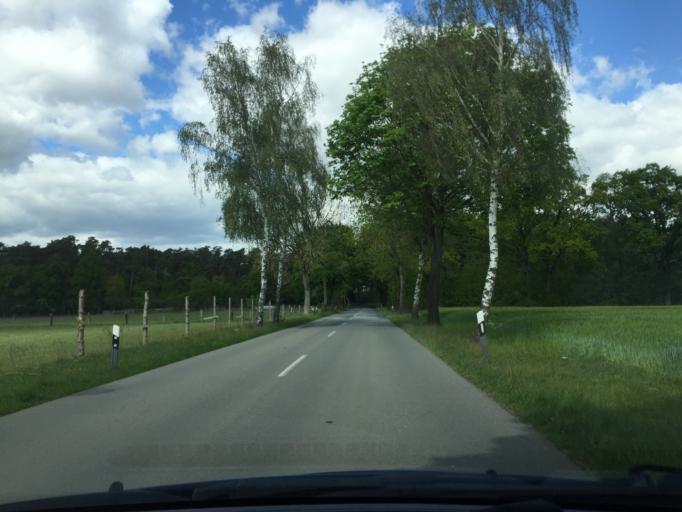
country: DE
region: Lower Saxony
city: Suderburg
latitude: 52.9229
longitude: 10.4990
